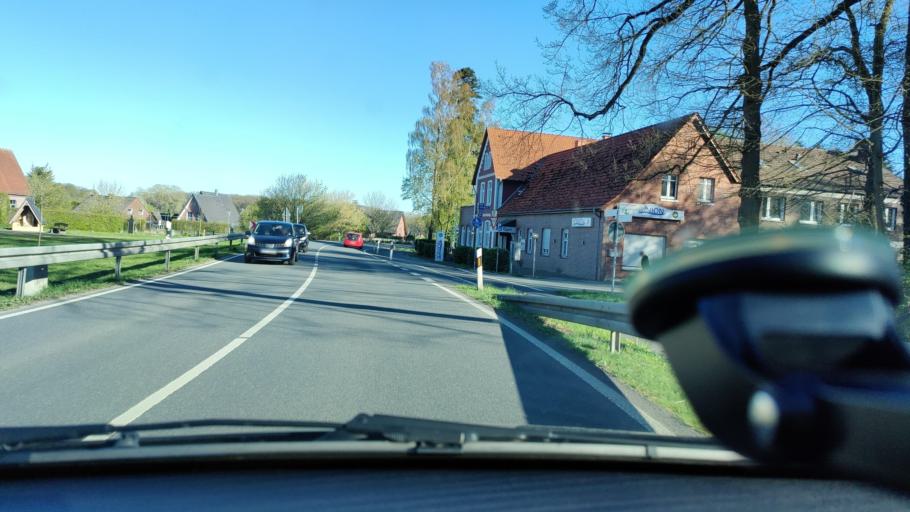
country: DE
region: North Rhine-Westphalia
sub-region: Regierungsbezirk Munster
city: Coesfeld
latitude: 51.9666
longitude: 7.1580
